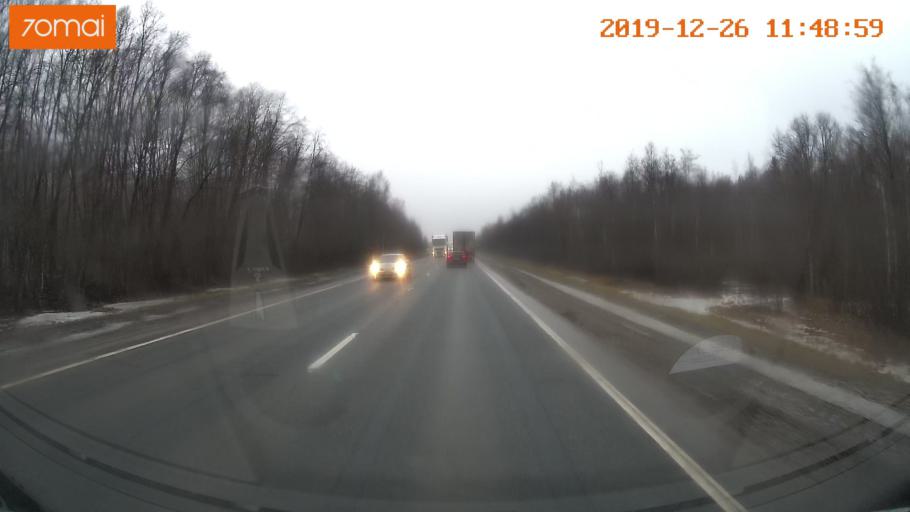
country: RU
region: Vologda
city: Sheksna
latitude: 59.2452
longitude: 38.4274
